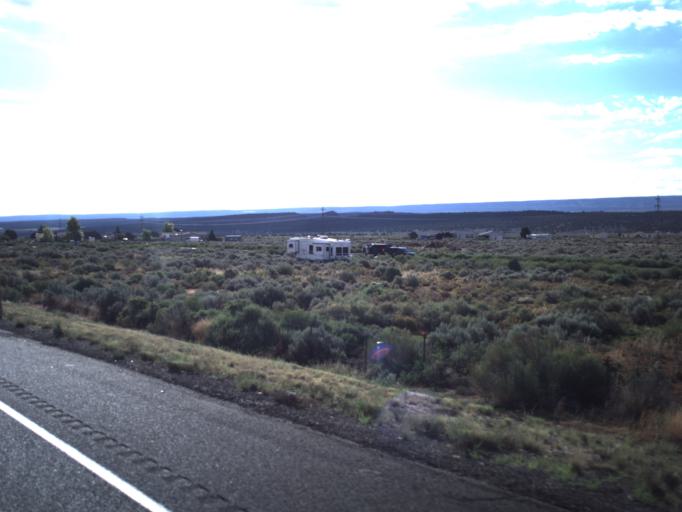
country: US
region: Utah
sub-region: Kane County
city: Kanab
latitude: 37.0268
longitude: -112.4172
